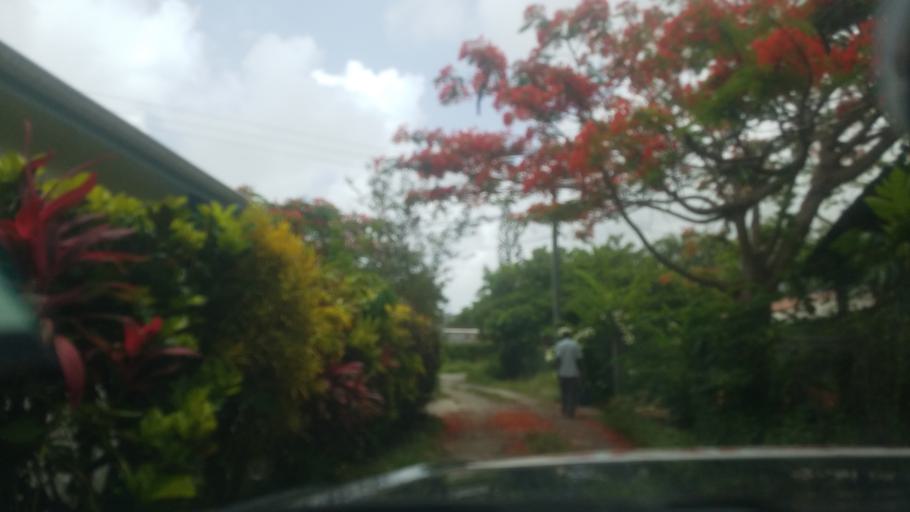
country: LC
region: Laborie Quarter
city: Laborie
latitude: 13.7608
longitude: -60.9741
